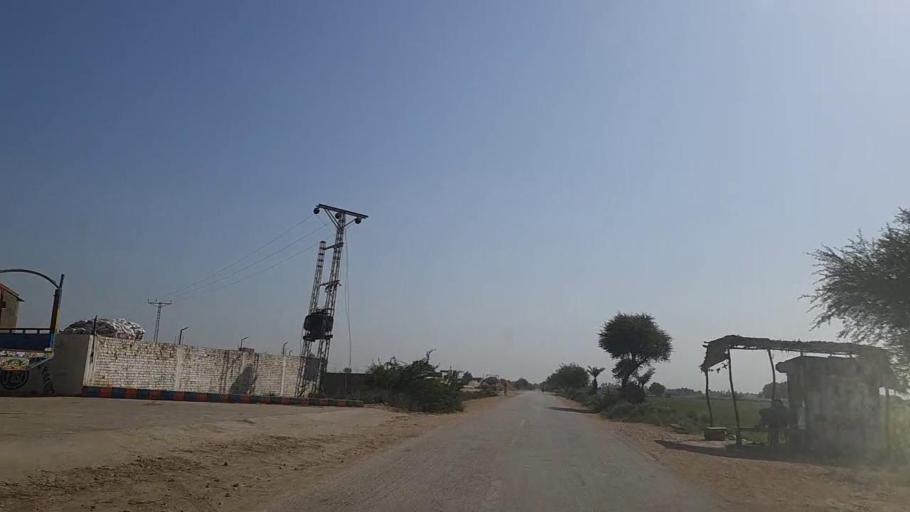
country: PK
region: Sindh
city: Mirpur Batoro
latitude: 24.6133
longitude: 68.2957
